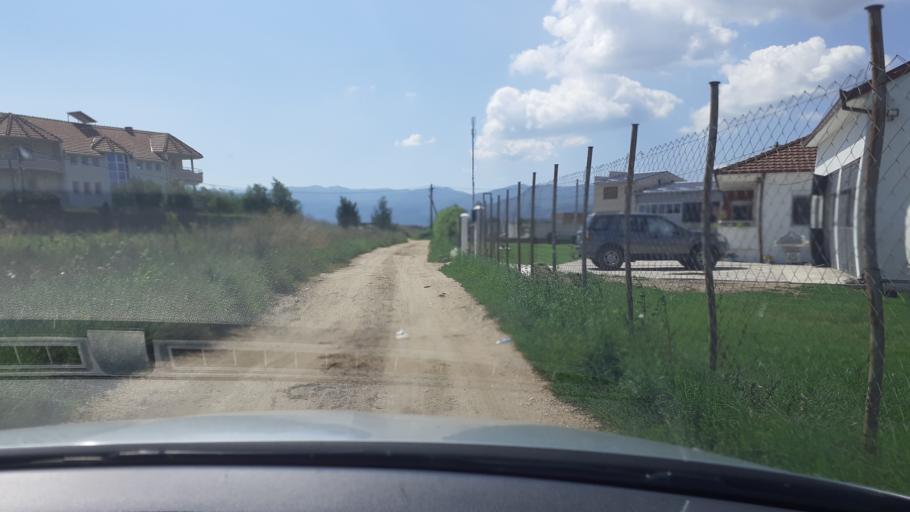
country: MK
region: Vasilevo
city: Vasilevo
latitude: 41.4684
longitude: 22.6425
